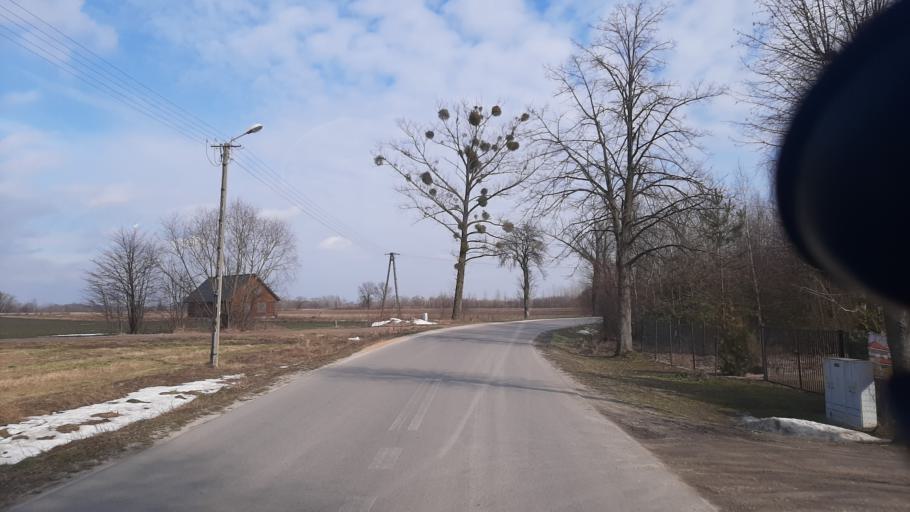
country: PL
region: Lublin Voivodeship
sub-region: Powiat lubartowski
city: Uscimow Stary
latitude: 51.4805
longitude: 22.9340
